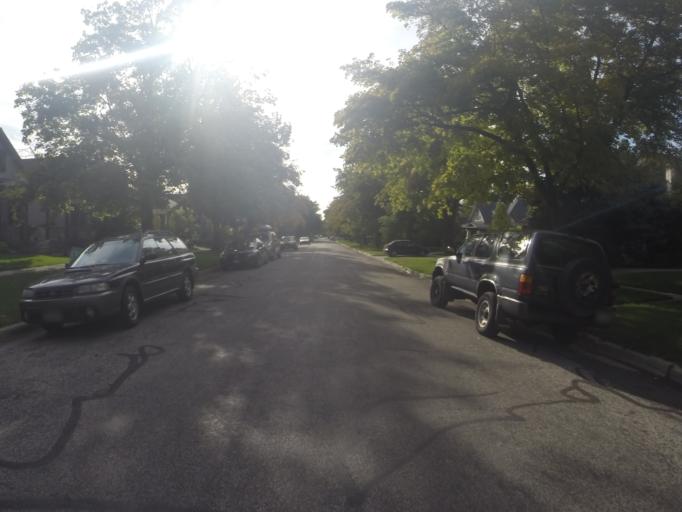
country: US
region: Utah
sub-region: Salt Lake County
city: Salt Lake City
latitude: 40.7439
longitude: -111.8624
